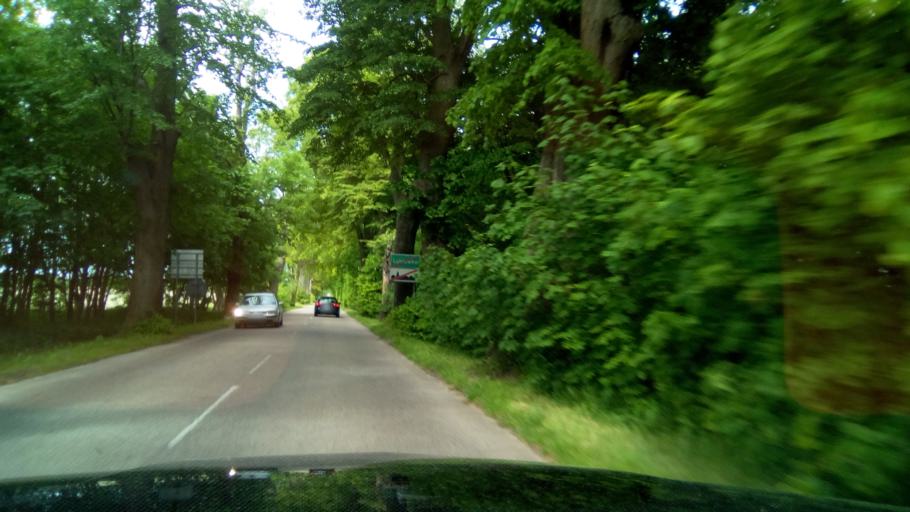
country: PL
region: Pomeranian Voivodeship
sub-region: Powiat wejherowski
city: Choczewo
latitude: 54.7592
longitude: 17.9291
